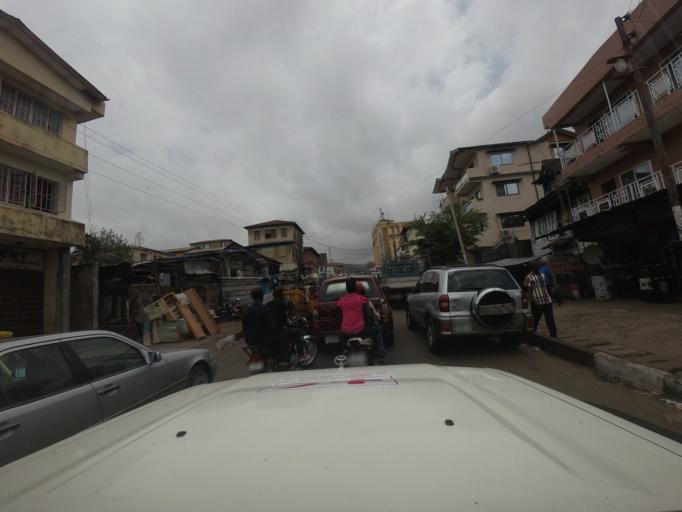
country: SL
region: Western Area
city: Freetown
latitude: 8.4851
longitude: -13.2389
